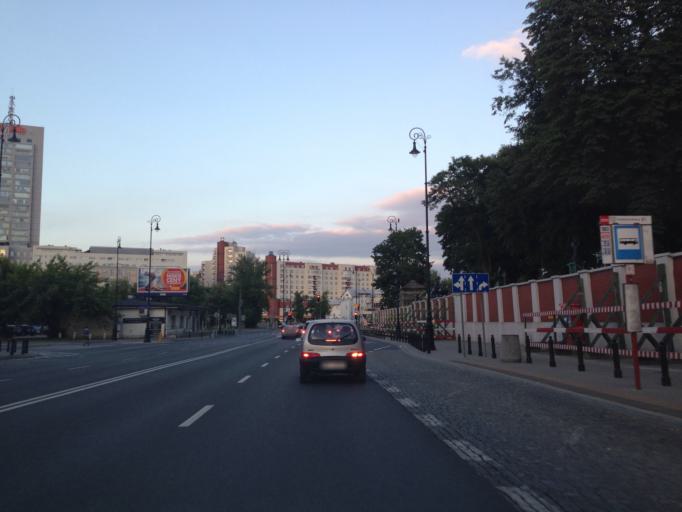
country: PL
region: Masovian Voivodeship
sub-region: Warszawa
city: Wola
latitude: 52.2534
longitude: 20.9793
